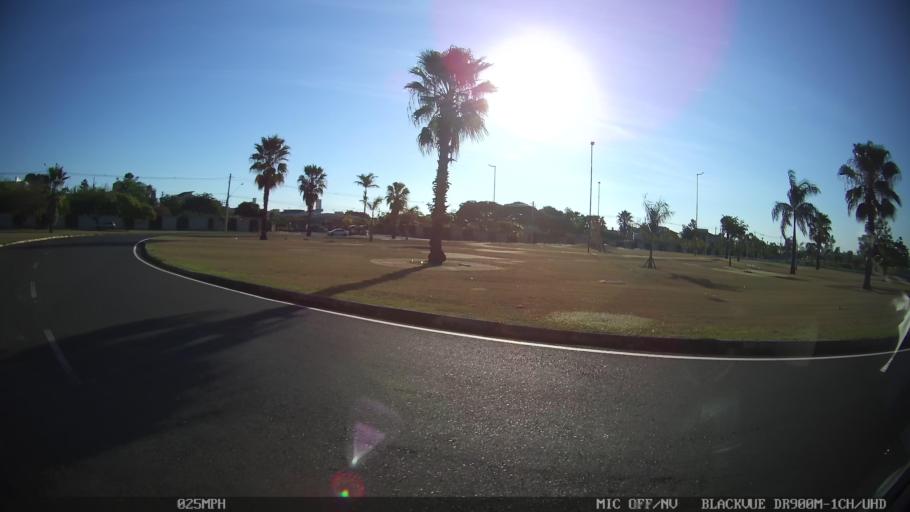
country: BR
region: Sao Paulo
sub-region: Sao Jose Do Rio Preto
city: Sao Jose do Rio Preto
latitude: -20.8599
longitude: -49.4117
